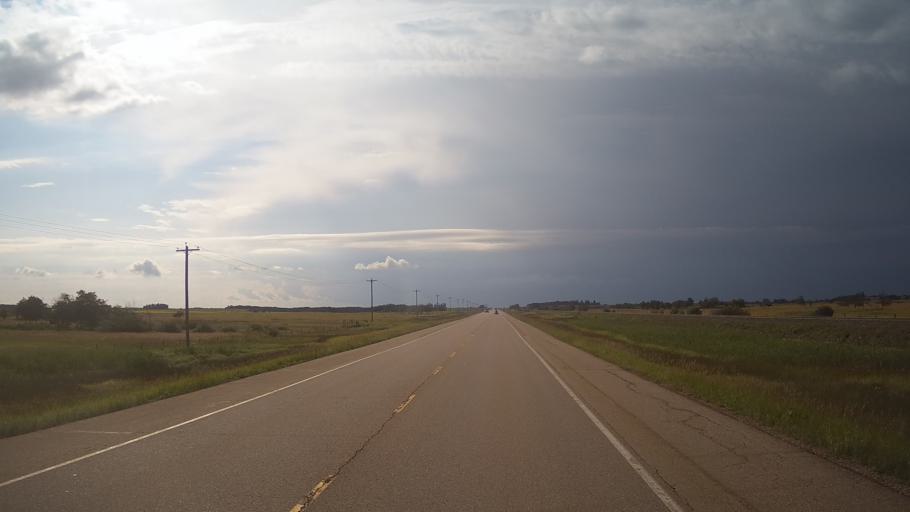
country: CA
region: Alberta
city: Viking
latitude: 53.1534
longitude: -111.9799
